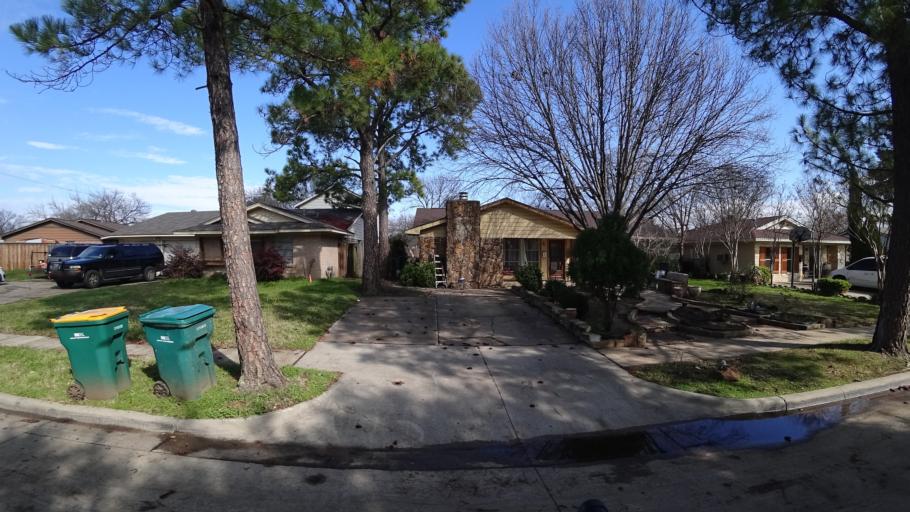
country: US
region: Texas
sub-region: Denton County
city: Lewisville
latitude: 33.0316
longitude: -96.9974
